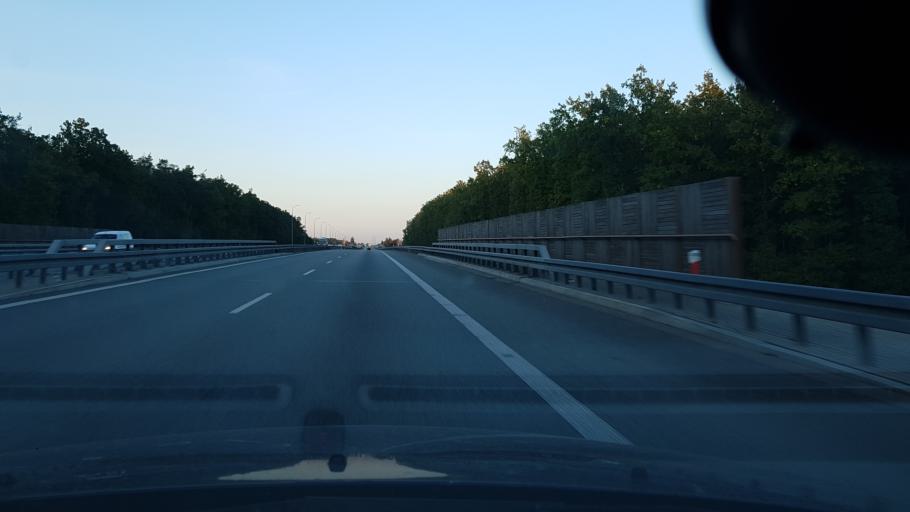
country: PL
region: Lodz Voivodeship
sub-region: Powiat rawski
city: Rawa Mazowiecka
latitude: 51.7284
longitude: 20.2276
